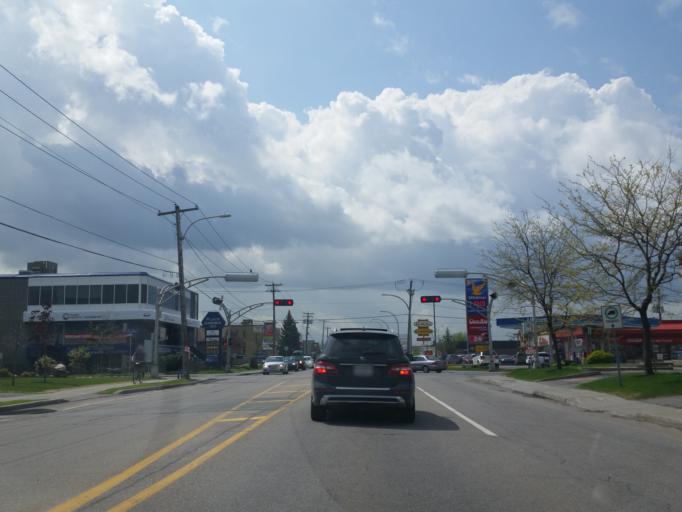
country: CA
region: Quebec
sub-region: Outaouais
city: Gatineau
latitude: 45.4821
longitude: -75.7017
